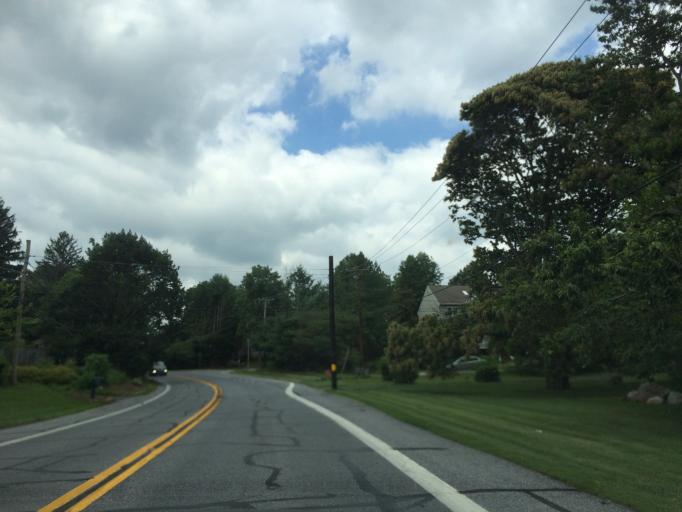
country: US
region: Maryland
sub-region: Howard County
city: Columbia
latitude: 39.3015
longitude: -76.8613
